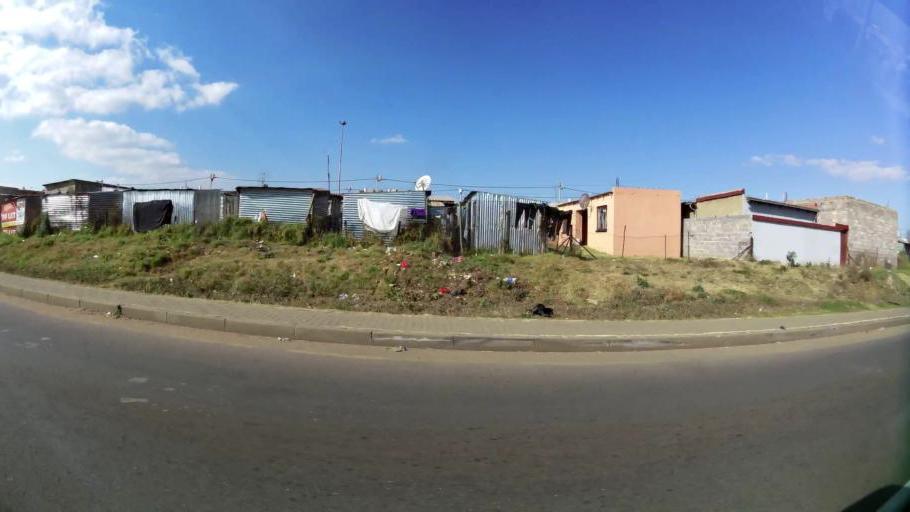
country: ZA
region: Gauteng
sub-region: City of Johannesburg Metropolitan Municipality
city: Soweto
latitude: -26.2720
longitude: 27.8906
